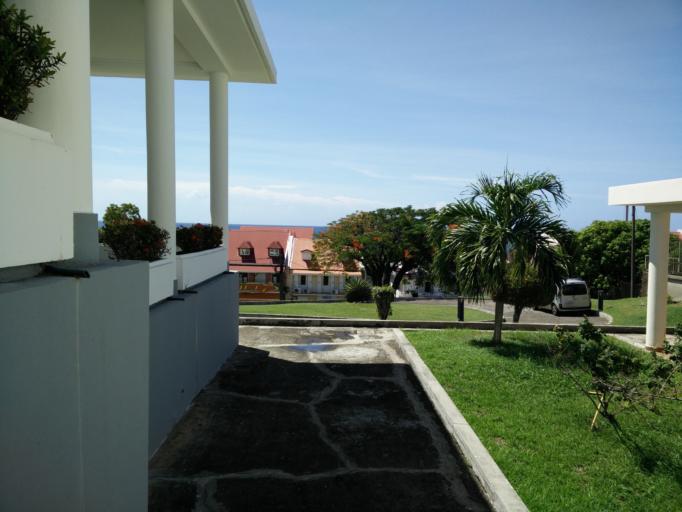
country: GP
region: Guadeloupe
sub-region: Guadeloupe
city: Basse-Terre
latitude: 15.9930
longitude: -61.7286
